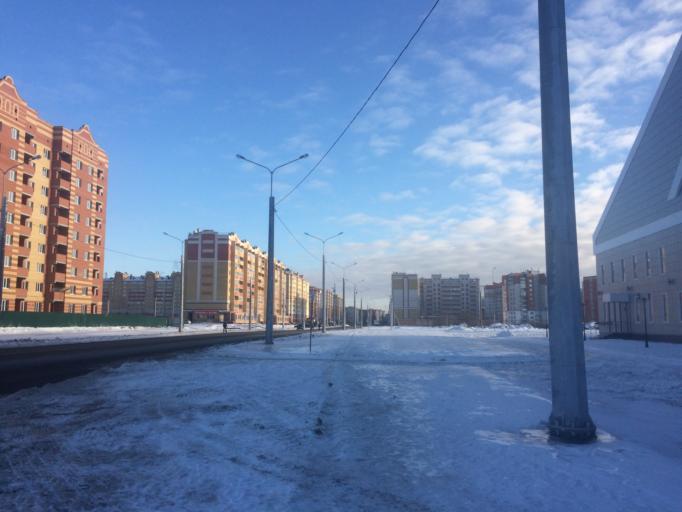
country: RU
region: Mariy-El
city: Yoshkar-Ola
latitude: 56.6407
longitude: 47.9169
